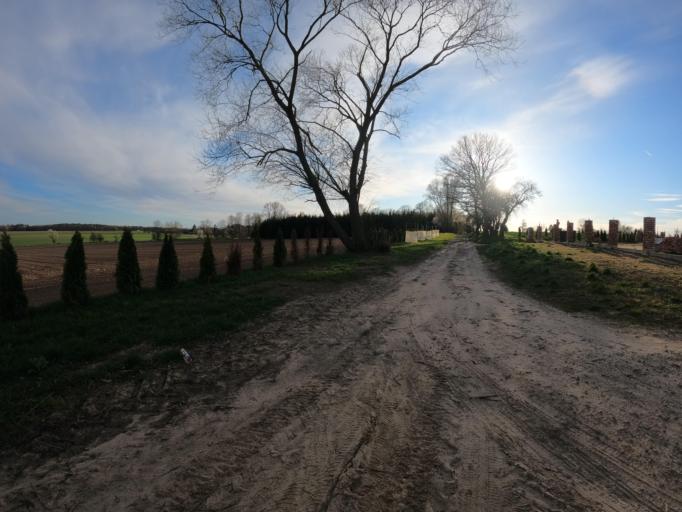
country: PL
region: West Pomeranian Voivodeship
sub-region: Powiat gryficki
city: Brojce
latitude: 53.9000
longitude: 15.2899
